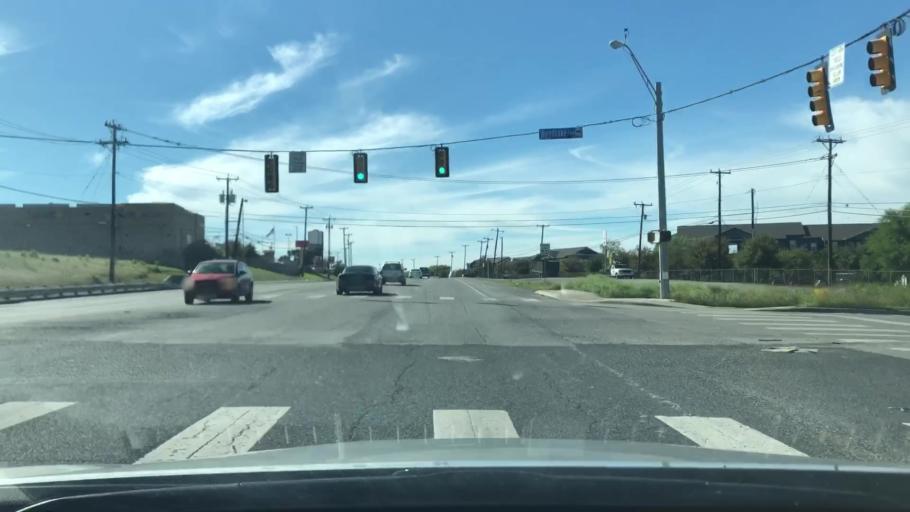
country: US
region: Texas
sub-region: Bexar County
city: Windcrest
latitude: 29.4858
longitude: -98.3471
